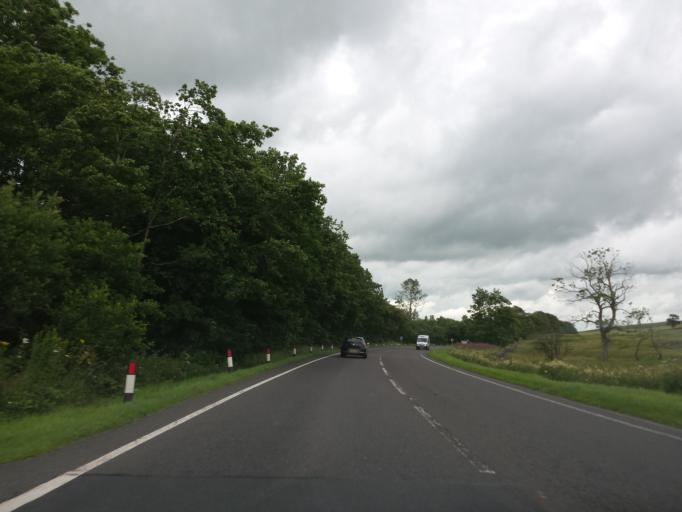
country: GB
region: Scotland
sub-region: Dumfries and Galloway
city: Dalbeattie
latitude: 55.0192
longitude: -3.8570
